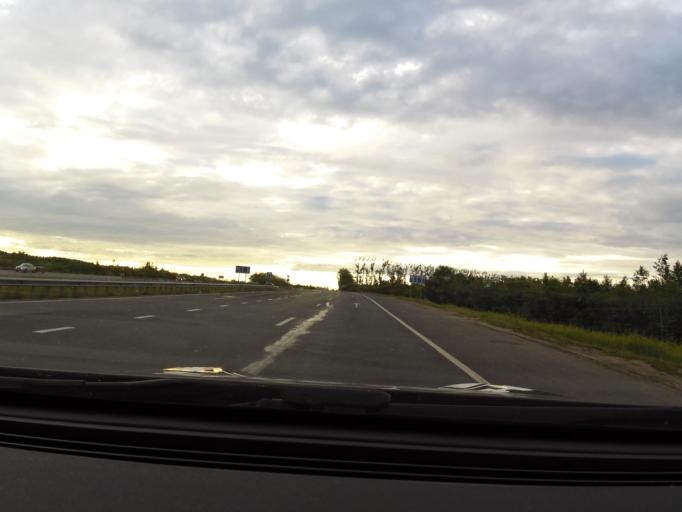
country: RU
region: Chuvashia
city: Tsivil'sk
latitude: 55.9401
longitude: 47.3846
